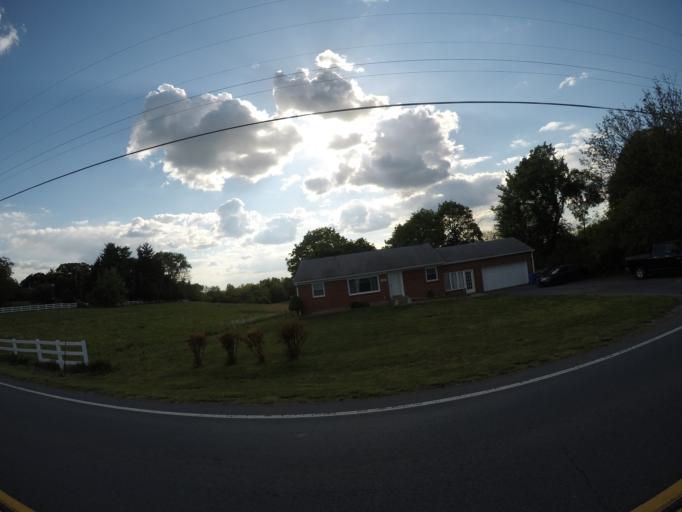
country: US
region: Maryland
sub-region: Montgomery County
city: Damascus
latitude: 39.3122
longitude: -77.1965
